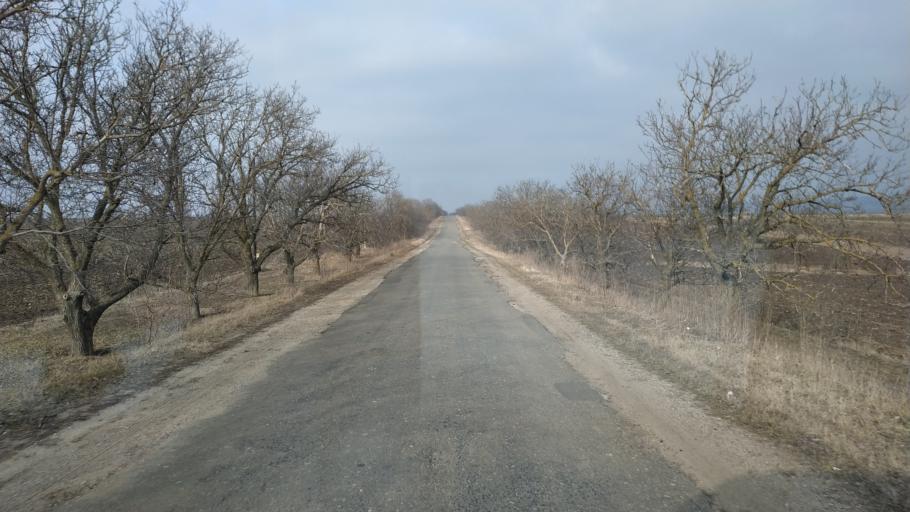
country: MD
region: Hincesti
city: Dancu
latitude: 46.8569
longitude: 28.2887
